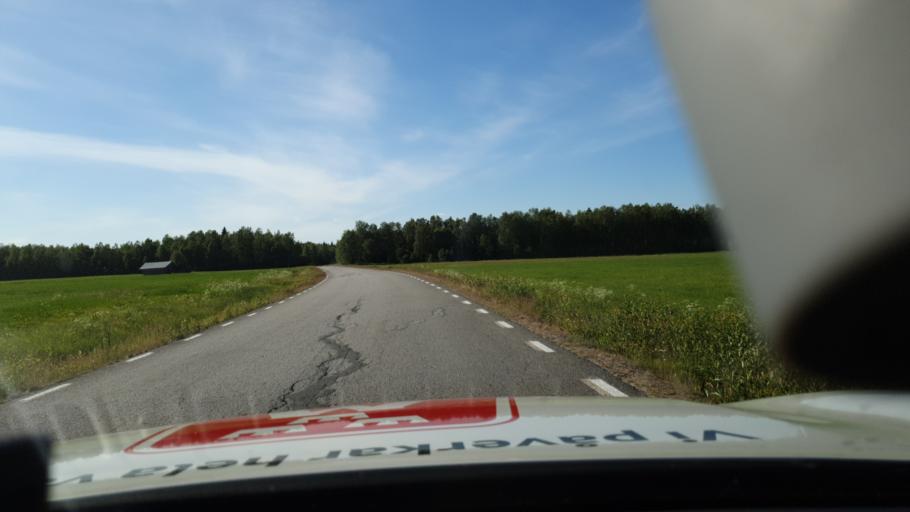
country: SE
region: Norrbotten
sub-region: Kalix Kommun
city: Toere
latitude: 65.8821
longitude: 22.6646
